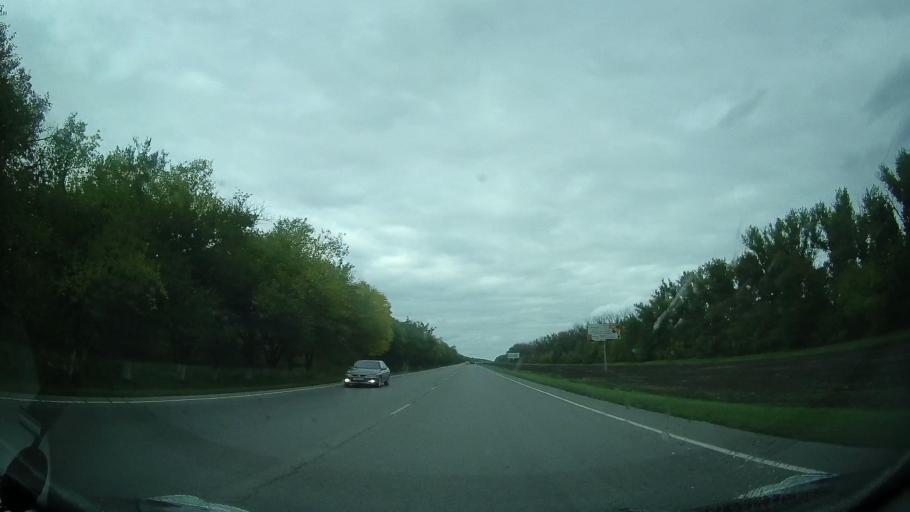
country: RU
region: Rostov
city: Yegorlykskaya
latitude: 46.6113
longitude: 40.6070
